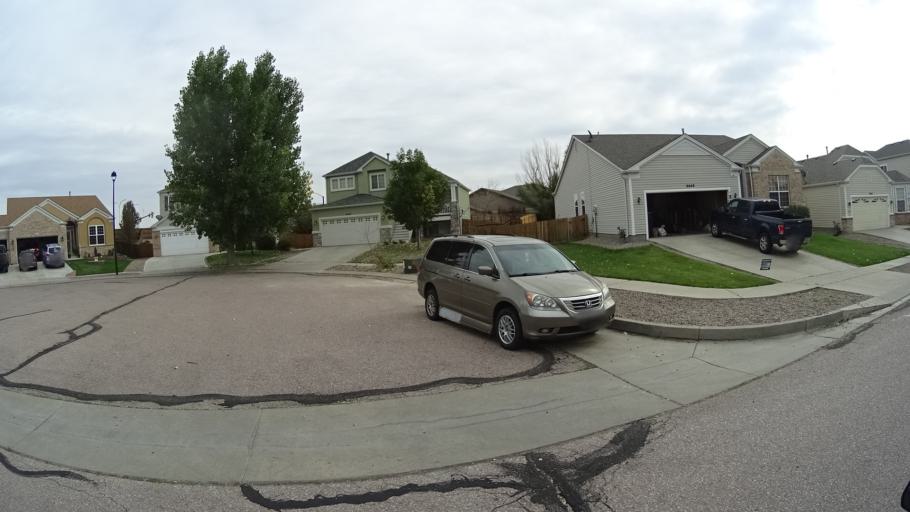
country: US
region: Colorado
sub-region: El Paso County
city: Cimarron Hills
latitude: 38.9253
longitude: -104.7003
